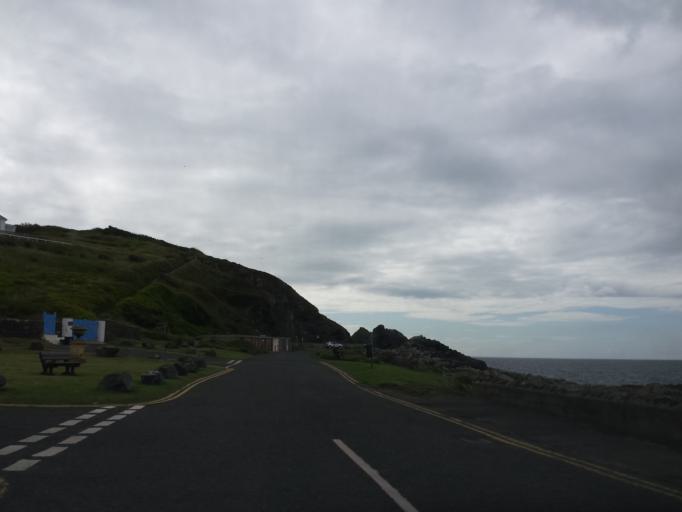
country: GB
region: Scotland
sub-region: Dumfries and Galloway
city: Stranraer
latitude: 54.8397
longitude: -5.1168
